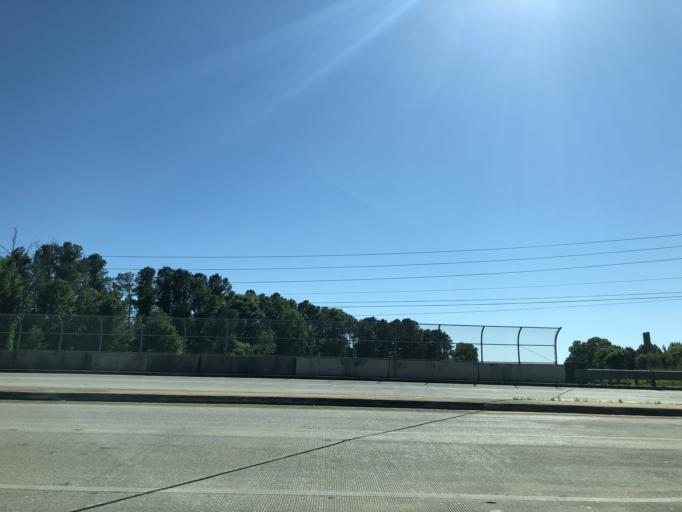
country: US
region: Georgia
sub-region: Clarke County
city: Country Club Estates
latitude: 33.9722
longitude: -83.4123
